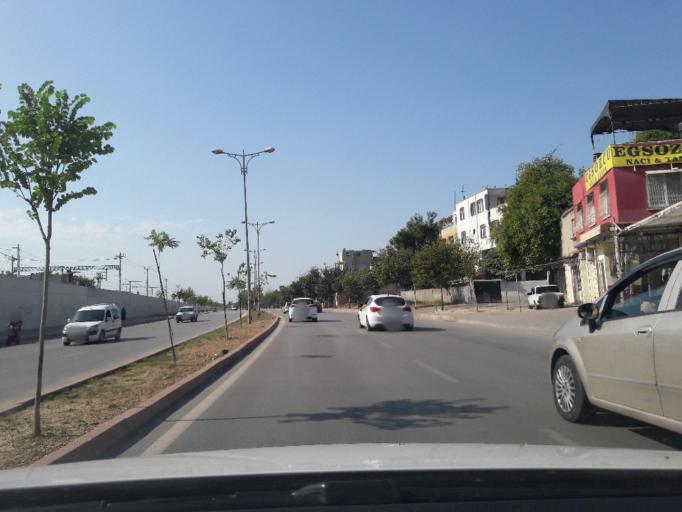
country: TR
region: Adana
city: Seyhan
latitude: 37.0030
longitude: 35.3102
